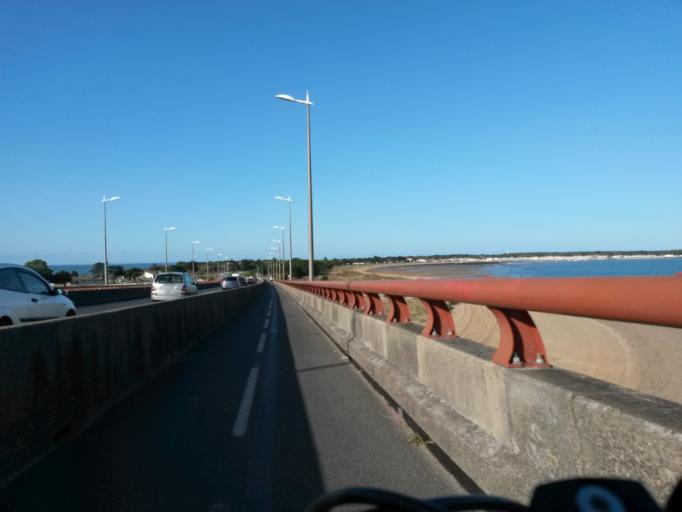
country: FR
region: Poitou-Charentes
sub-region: Departement de la Charente-Maritime
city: Rivedoux-Plage
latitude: 46.1655
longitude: -1.2538
